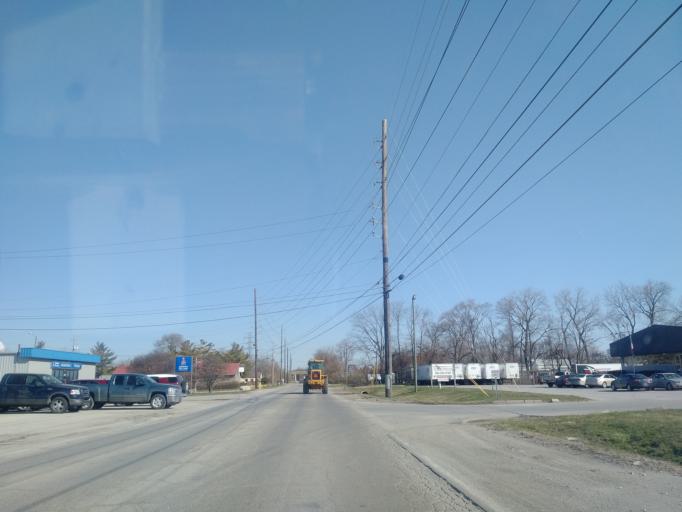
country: US
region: Indiana
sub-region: Marion County
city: Indianapolis
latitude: 39.7323
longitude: -86.1683
